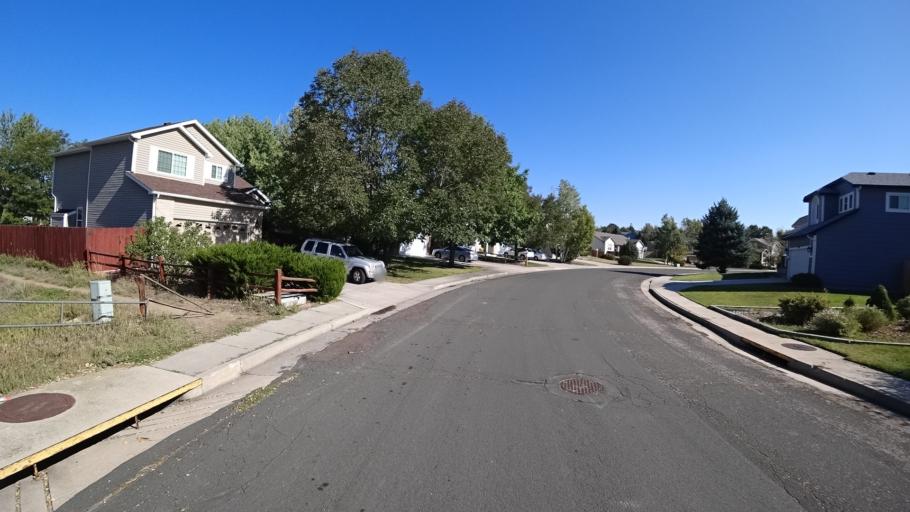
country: US
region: Colorado
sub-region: El Paso County
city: Cimarron Hills
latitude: 38.8795
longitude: -104.7051
